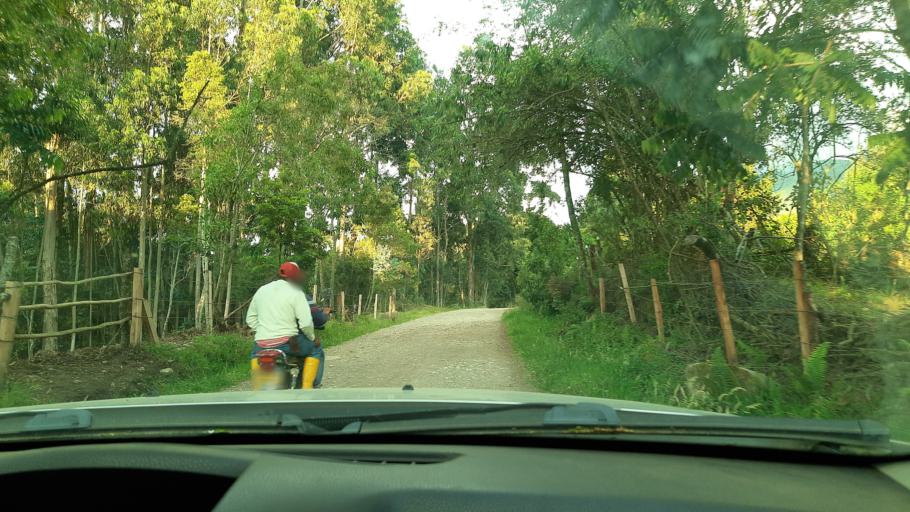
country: CO
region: Boyaca
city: La Capilla
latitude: 5.7129
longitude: -73.4785
